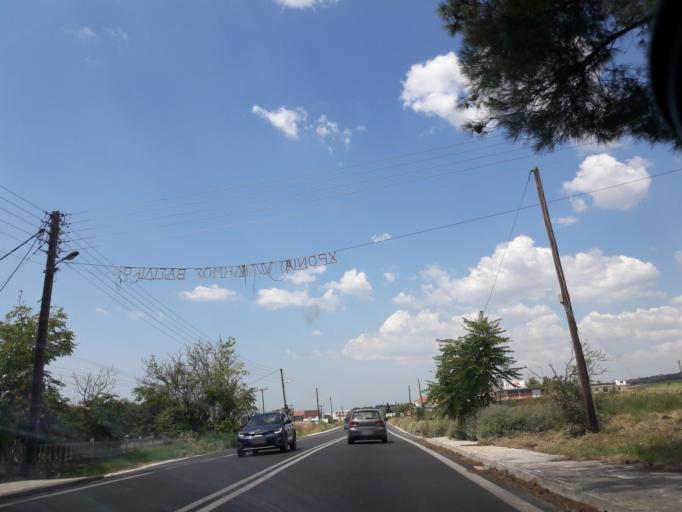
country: GR
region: Central Macedonia
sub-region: Nomos Thessalonikis
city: Agia Paraskevi
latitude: 40.5138
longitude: 23.0744
